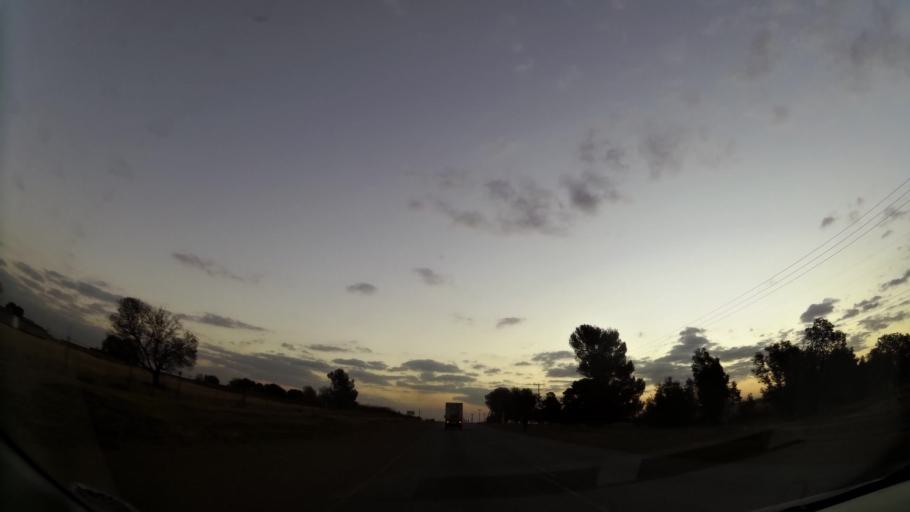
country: ZA
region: Gauteng
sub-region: West Rand District Municipality
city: Krugersdorp
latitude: -26.0712
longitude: 27.6689
